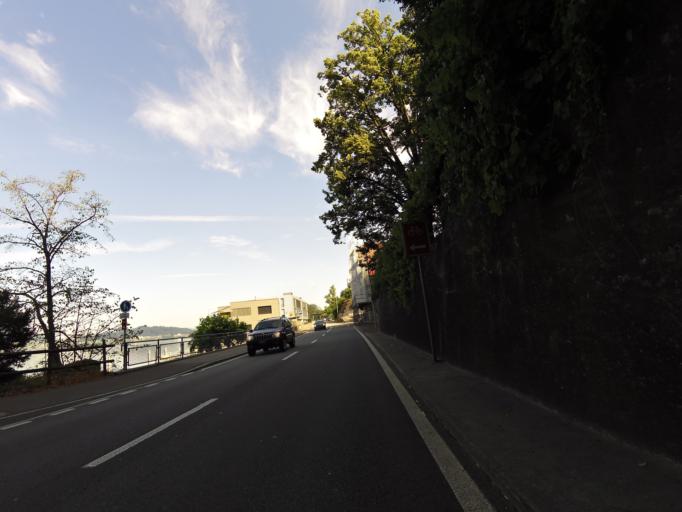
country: CH
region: Zug
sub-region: Zug
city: Walchwil
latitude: 47.1141
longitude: 8.5007
